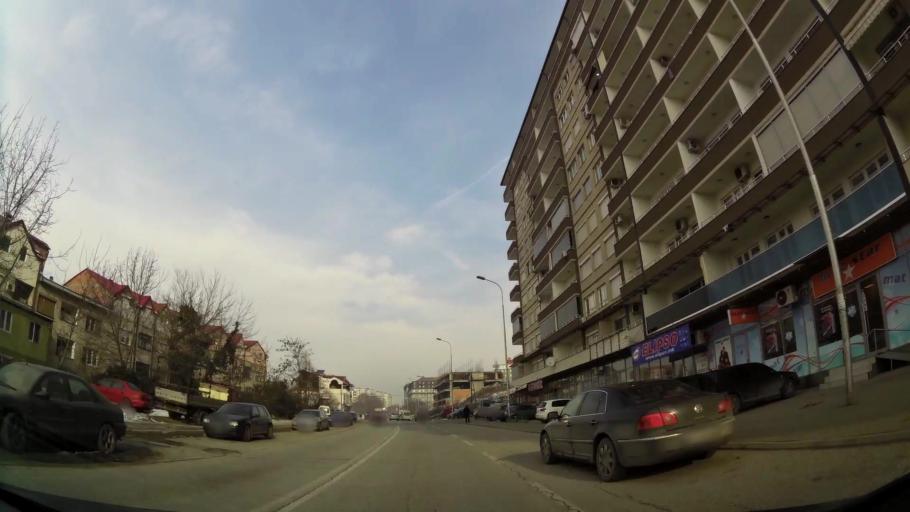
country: MK
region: Cair
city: Cair
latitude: 42.0172
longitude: 21.4360
